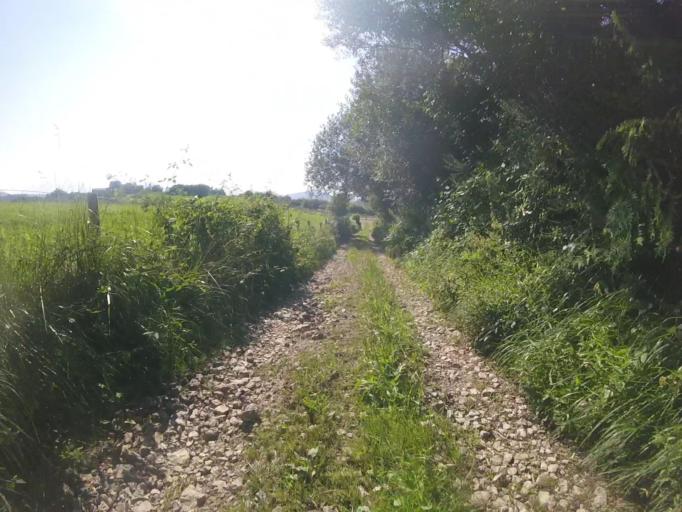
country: ES
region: Basque Country
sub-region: Provincia de Guipuzcoa
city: Astigarraga
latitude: 43.2583
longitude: -1.9380
